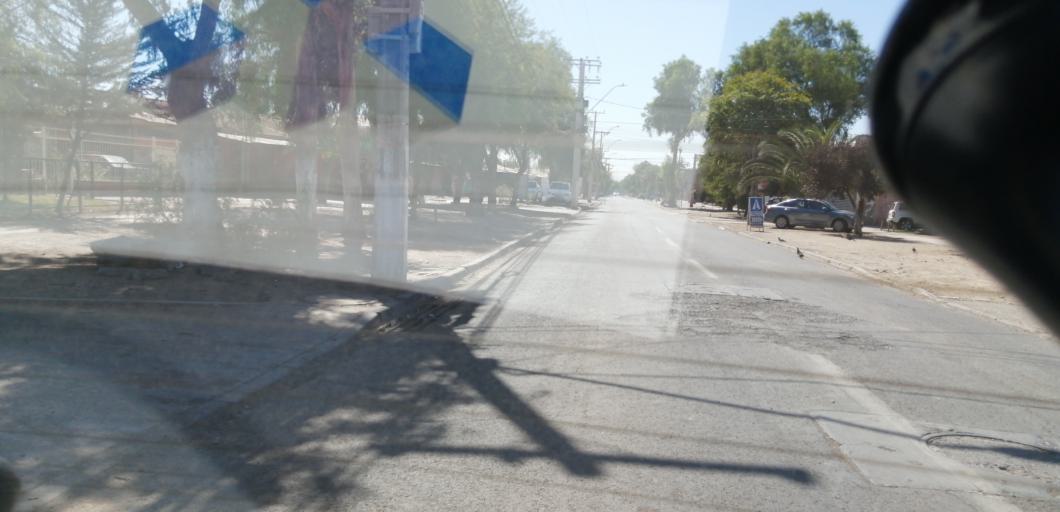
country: CL
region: Santiago Metropolitan
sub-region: Provincia de Santiago
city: Lo Prado
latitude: -33.4370
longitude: -70.7584
